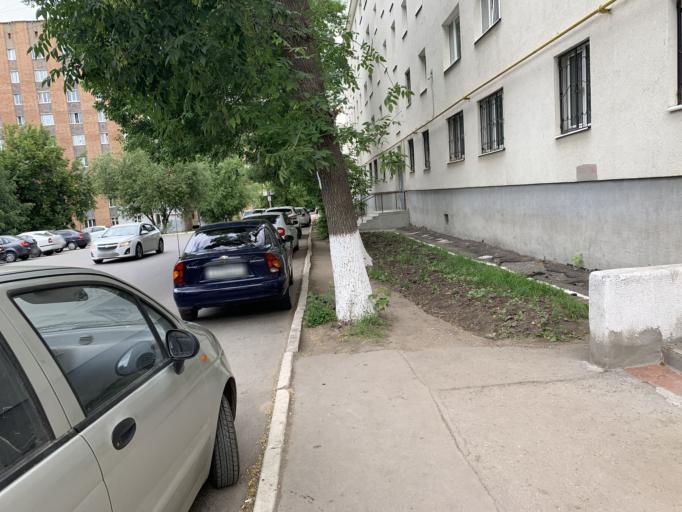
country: RU
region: Samara
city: Samara
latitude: 53.2143
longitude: 50.1682
